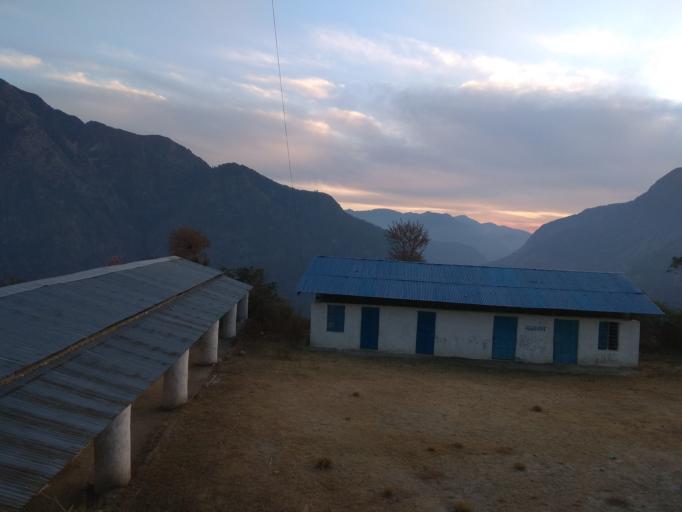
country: NP
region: Far Western
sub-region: Seti Zone
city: Achham
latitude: 29.2421
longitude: 81.6422
